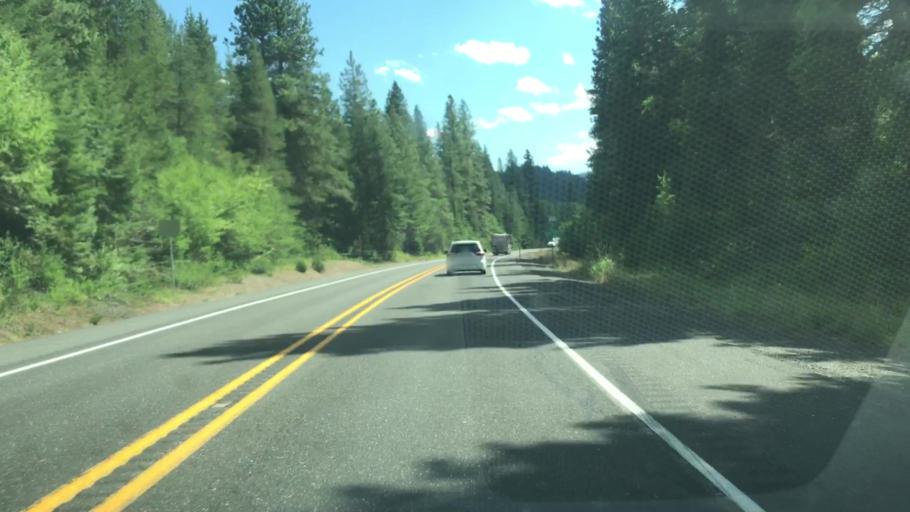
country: US
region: Washington
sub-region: Chelan County
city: Leavenworth
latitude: 47.7540
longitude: -120.7380
